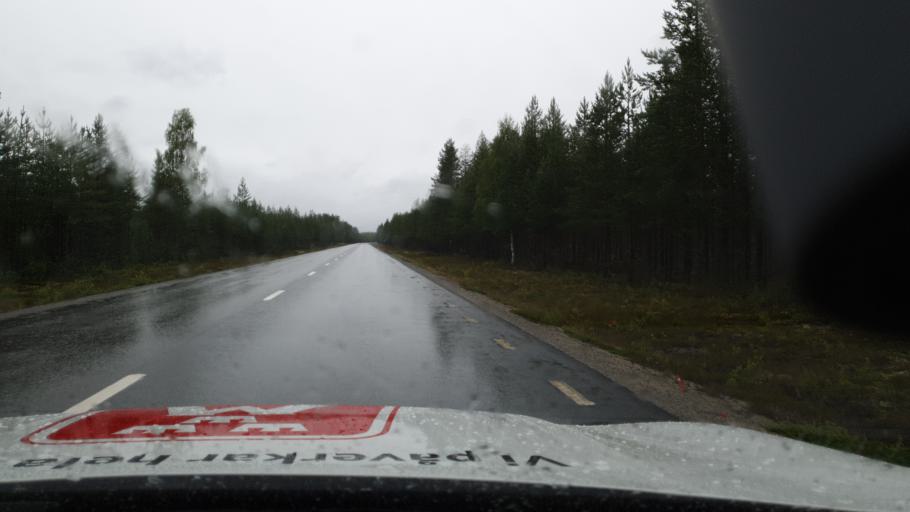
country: SE
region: Vaesterbotten
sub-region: Vindelns Kommun
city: Vindeln
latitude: 64.1602
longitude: 19.8288
